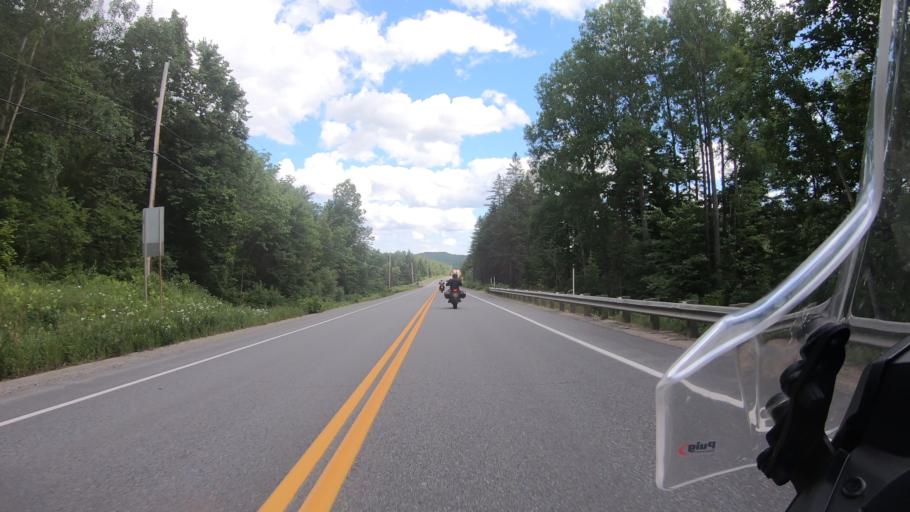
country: CA
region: Quebec
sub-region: Mauricie
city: Saint-Tite
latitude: 46.9906
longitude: -72.9136
